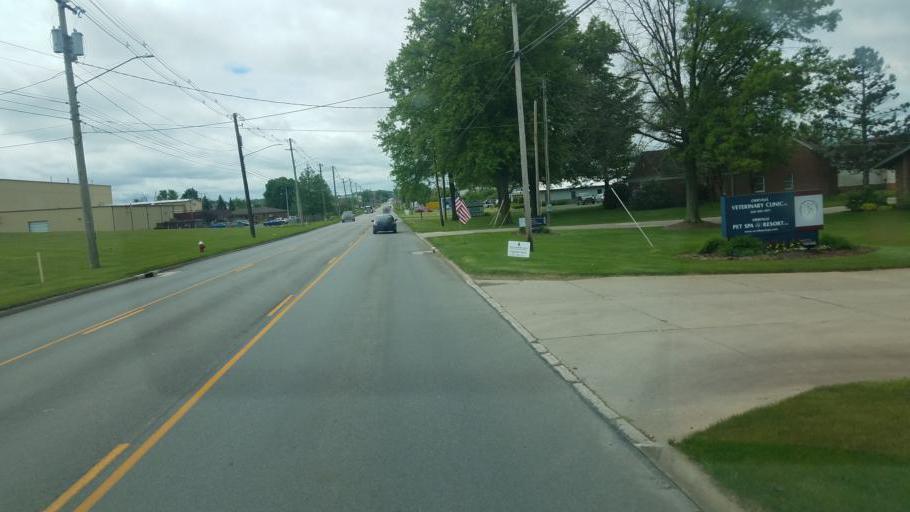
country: US
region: Ohio
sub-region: Wayne County
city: Orrville
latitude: 40.8619
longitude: -81.7637
